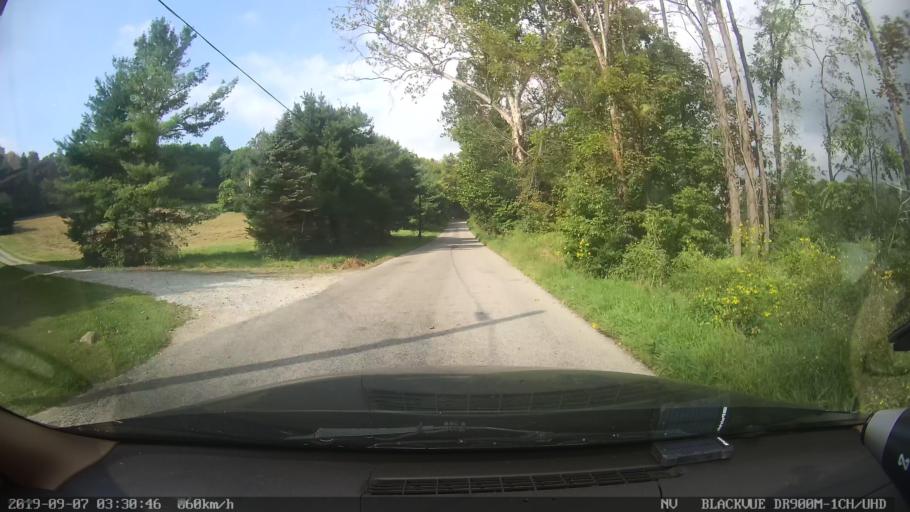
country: US
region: Ohio
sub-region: Licking County
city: Granville
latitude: 40.1201
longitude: -82.5242
